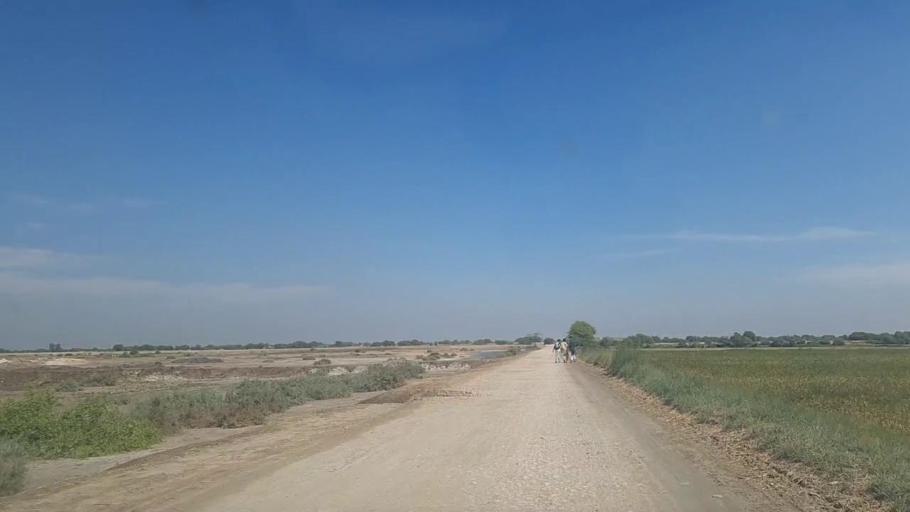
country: PK
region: Sindh
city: Mirpur Batoro
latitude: 24.7050
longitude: 68.2405
